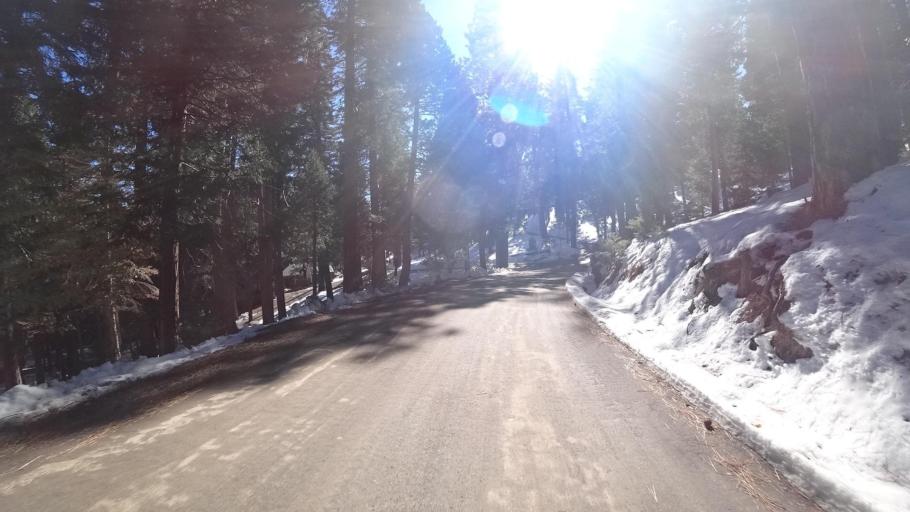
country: US
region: California
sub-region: Kern County
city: Alta Sierra
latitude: 35.7310
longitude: -118.5538
